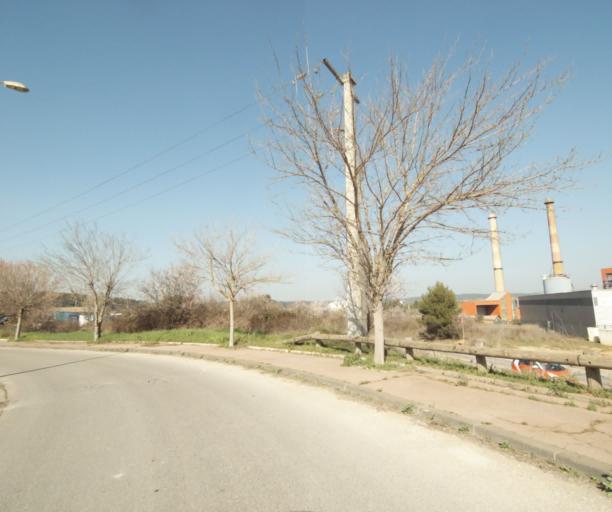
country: FR
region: Provence-Alpes-Cote d'Azur
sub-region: Departement des Bouches-du-Rhone
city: Gardanne
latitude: 43.4500
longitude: 5.4557
